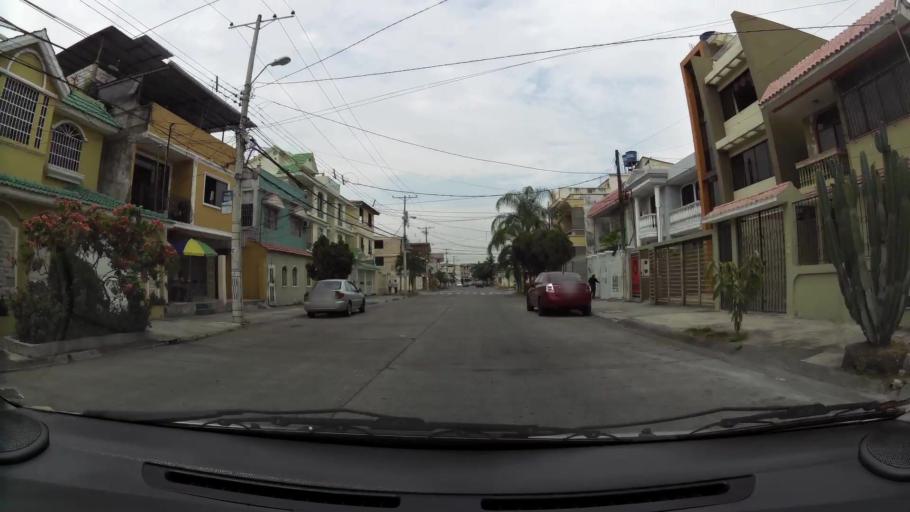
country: EC
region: Guayas
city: Eloy Alfaro
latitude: -2.1446
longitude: -79.8910
